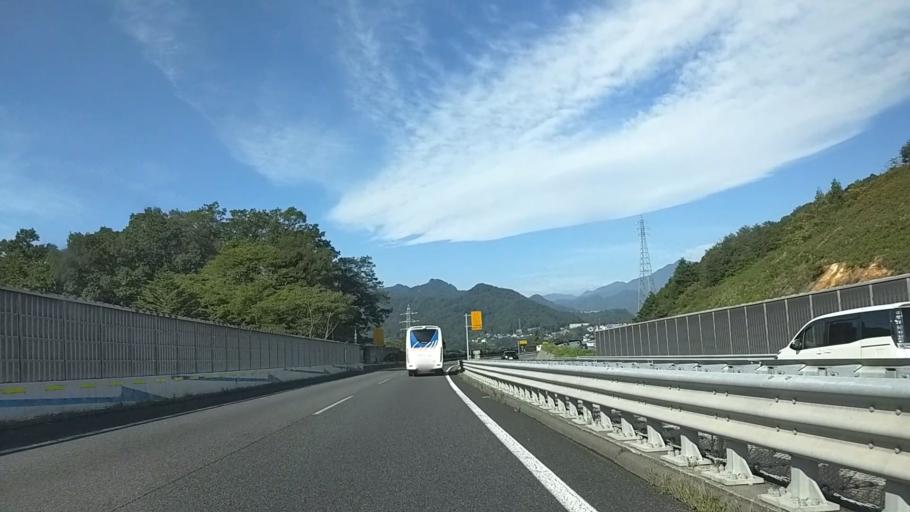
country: JP
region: Yamanashi
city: Otsuki
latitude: 35.6104
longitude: 139.0135
